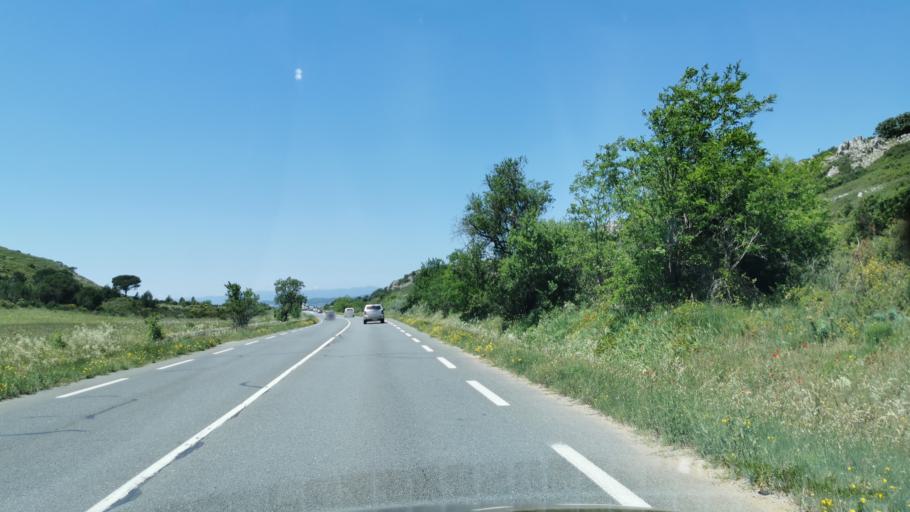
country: FR
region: Languedoc-Roussillon
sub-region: Departement de l'Aude
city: Nevian
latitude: 43.2044
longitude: 2.8885
